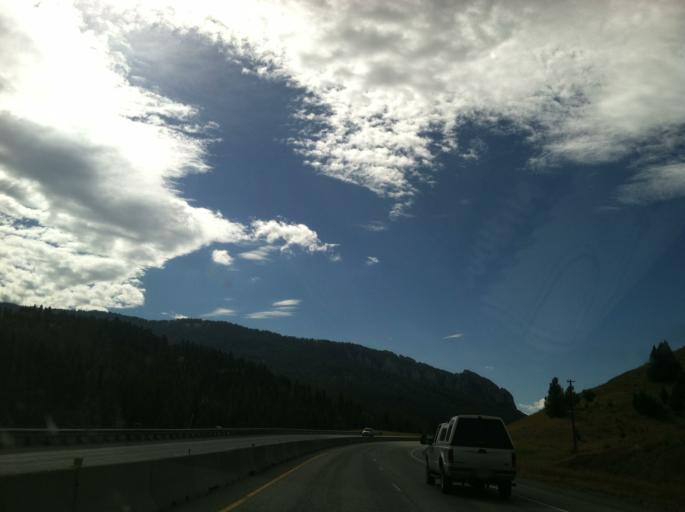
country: US
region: Montana
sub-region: Gallatin County
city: Bozeman
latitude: 45.6486
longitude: -110.8638
